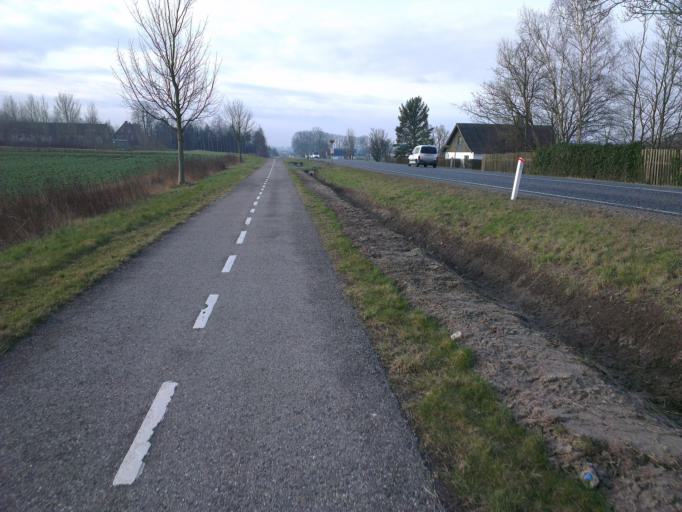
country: DK
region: Capital Region
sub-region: Frederikssund Kommune
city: Skibby
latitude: 55.7982
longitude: 11.9804
